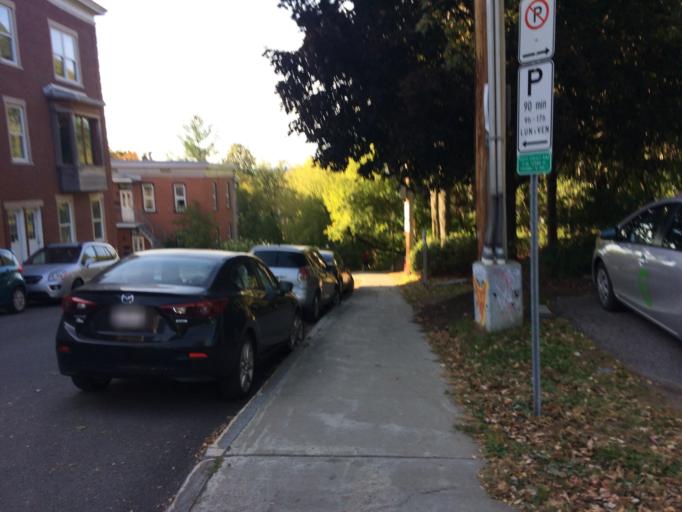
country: CA
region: Quebec
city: Quebec
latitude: 46.8053
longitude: -71.2333
